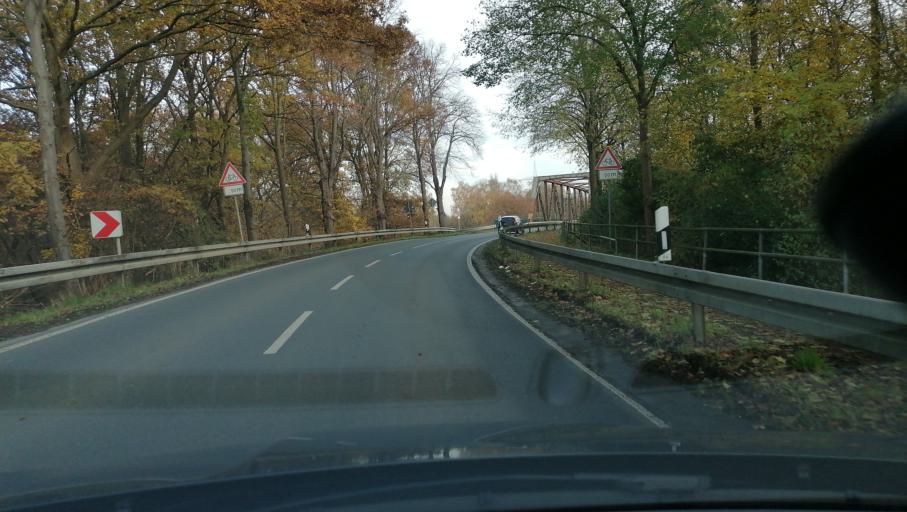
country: DE
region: North Rhine-Westphalia
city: Castrop-Rauxel
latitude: 51.5828
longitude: 7.2875
